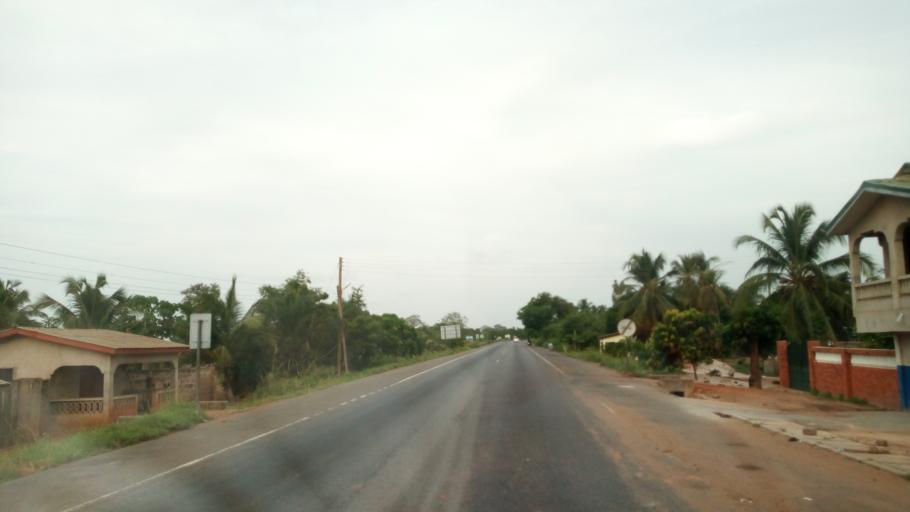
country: GH
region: Volta
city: Keta
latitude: 6.0521
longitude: 0.9745
